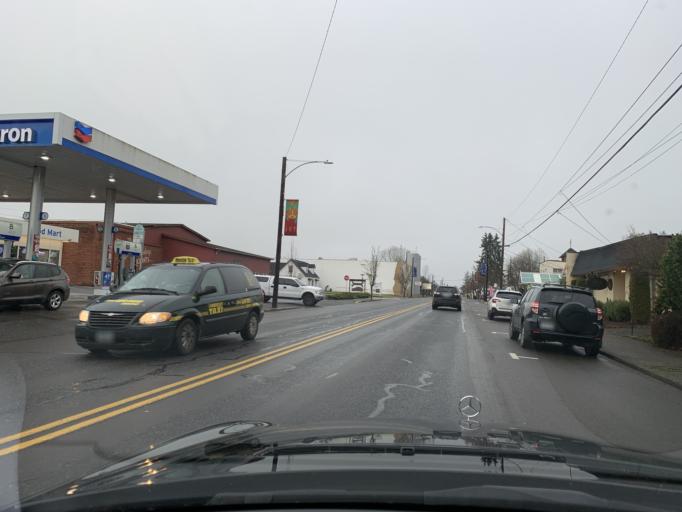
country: US
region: Washington
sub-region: Clark County
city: Battle Ground
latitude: 45.7809
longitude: -122.5323
